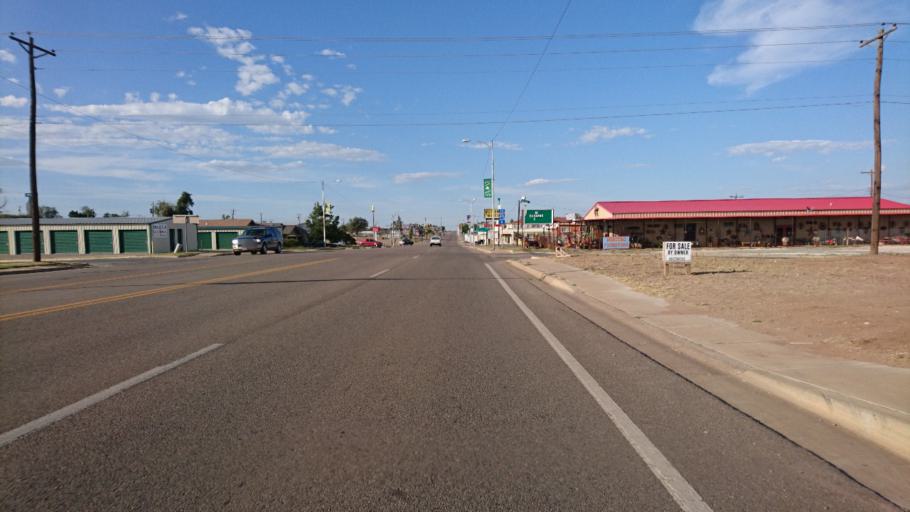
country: US
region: Texas
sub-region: Wheeler County
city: Shamrock
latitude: 35.2248
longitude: -100.2492
